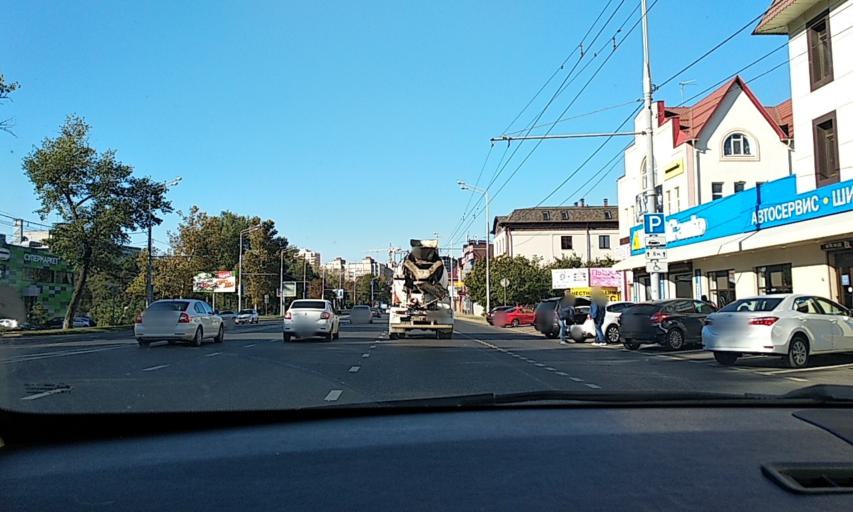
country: RU
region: Krasnodarskiy
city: Pashkovskiy
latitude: 45.0131
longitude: 39.0786
